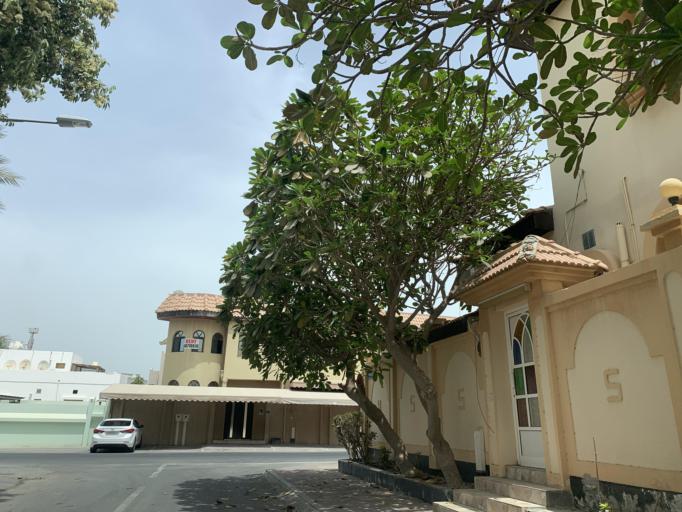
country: BH
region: Northern
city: Ar Rifa'
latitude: 26.1379
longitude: 50.5613
